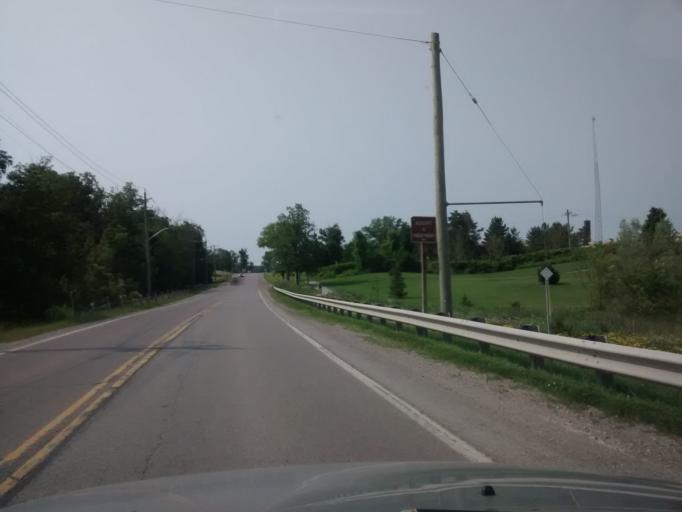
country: CA
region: Ontario
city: Ancaster
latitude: 42.9604
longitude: -79.8615
